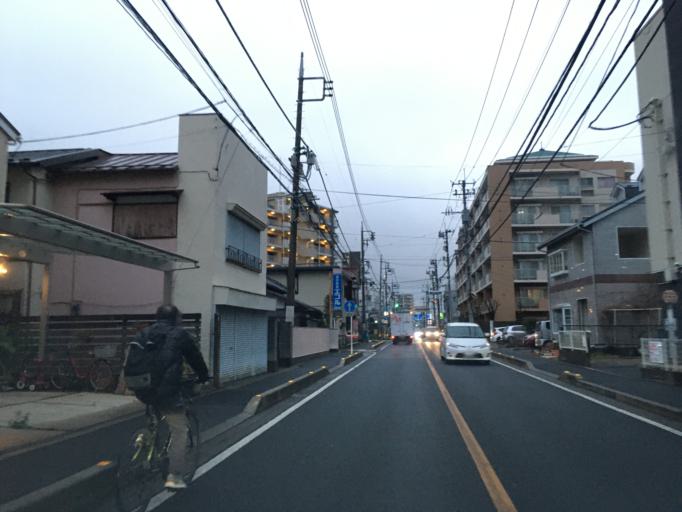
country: JP
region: Saitama
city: Wako
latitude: 35.7847
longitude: 139.6065
